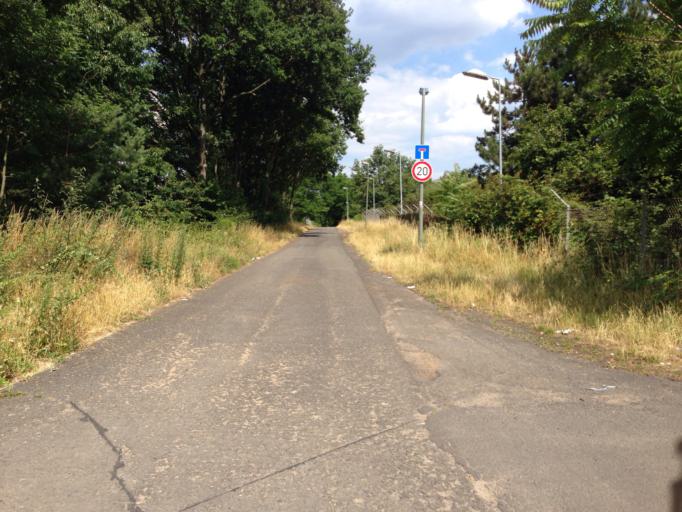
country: DE
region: Hesse
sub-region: Regierungsbezirk Darmstadt
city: Grosskrotzenburg
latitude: 50.1007
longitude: 8.9619
